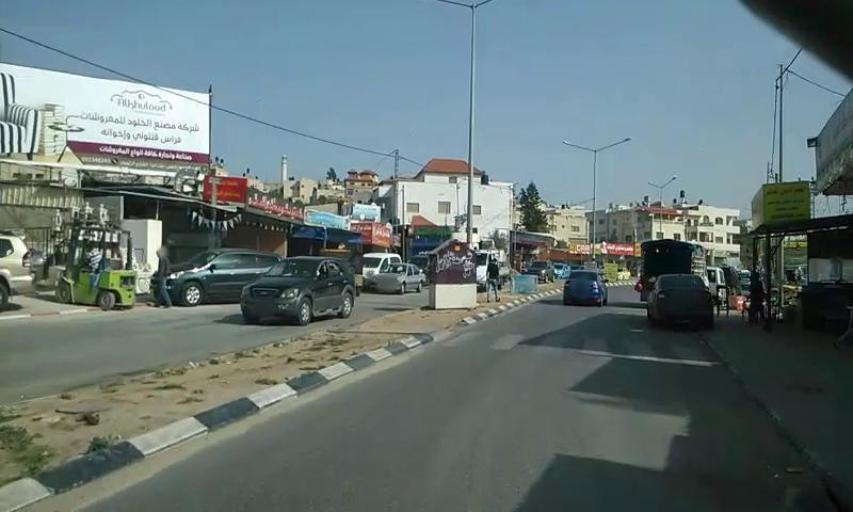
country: PS
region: West Bank
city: Dayr Sharaf
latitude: 32.2548
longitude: 35.1852
